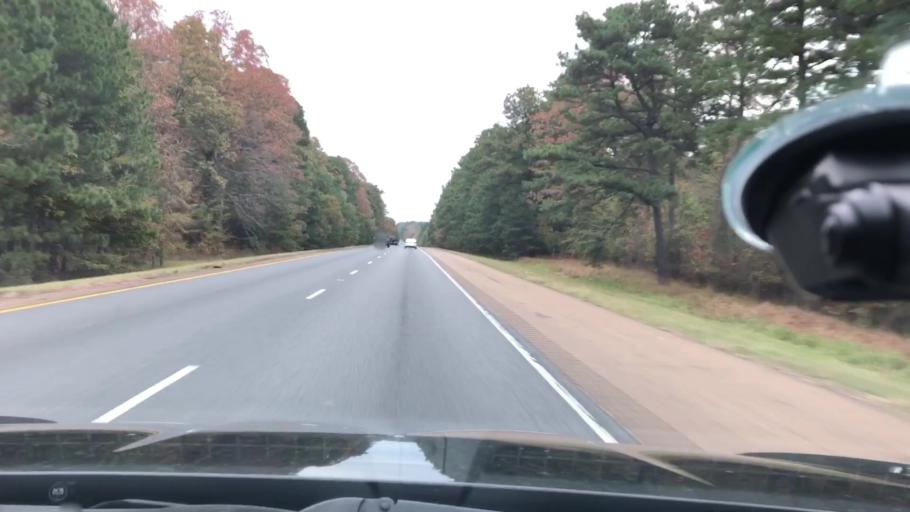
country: US
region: Arkansas
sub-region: Clark County
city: Gurdon
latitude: 33.9391
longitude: -93.2472
